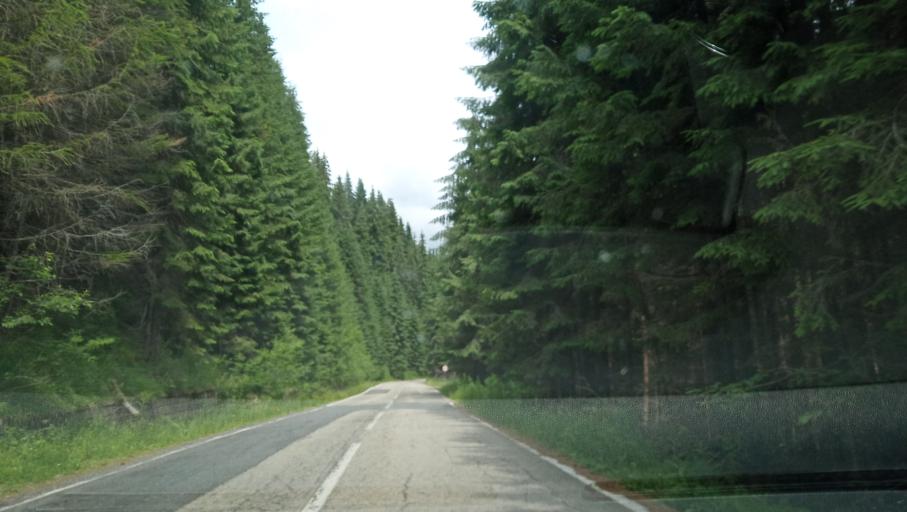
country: RO
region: Valcea
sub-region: Comuna Voineasa
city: Voineasa
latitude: 45.4219
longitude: 23.7527
